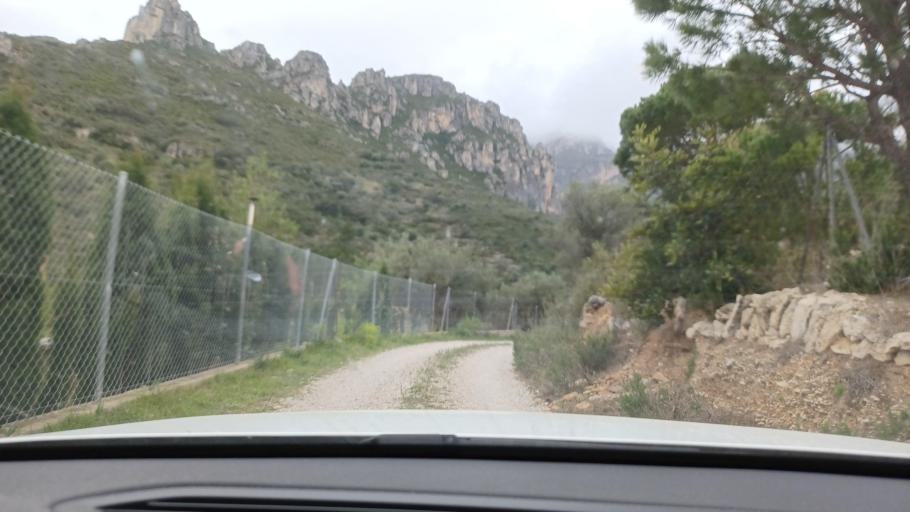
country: ES
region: Catalonia
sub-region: Provincia de Tarragona
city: Mas de Barberans
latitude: 40.8057
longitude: 0.3994
